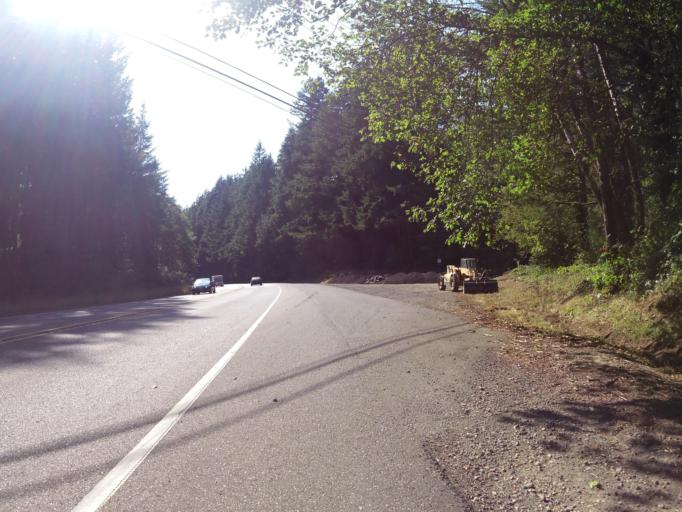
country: US
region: Oregon
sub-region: Douglas County
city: Reedsport
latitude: 43.6898
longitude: -124.1411
